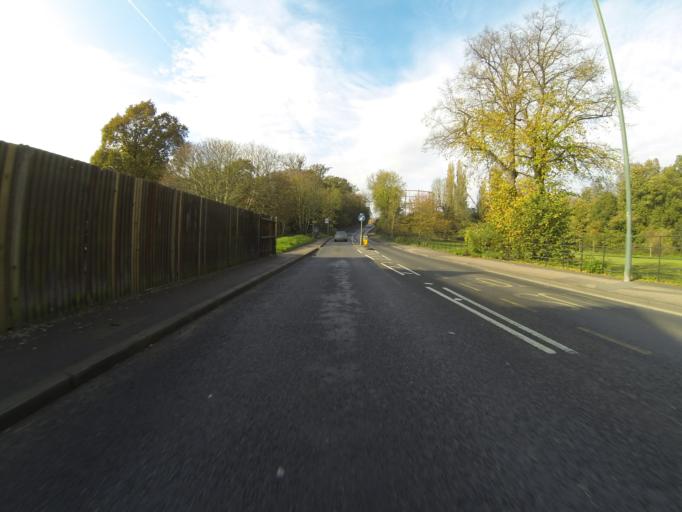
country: GB
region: England
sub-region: Greater London
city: Bexley
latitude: 51.4524
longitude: 0.1689
